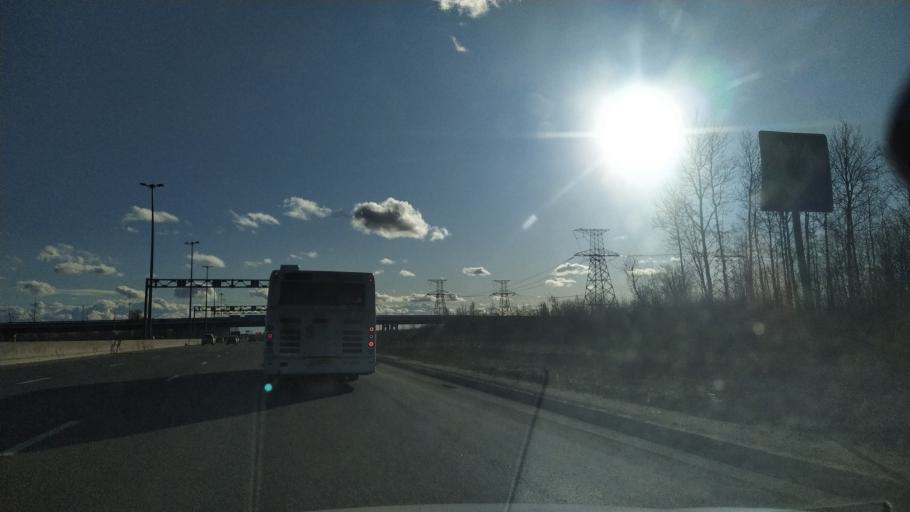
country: RU
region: St.-Petersburg
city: Aleksandrovskaya
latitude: 59.7205
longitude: 30.2845
